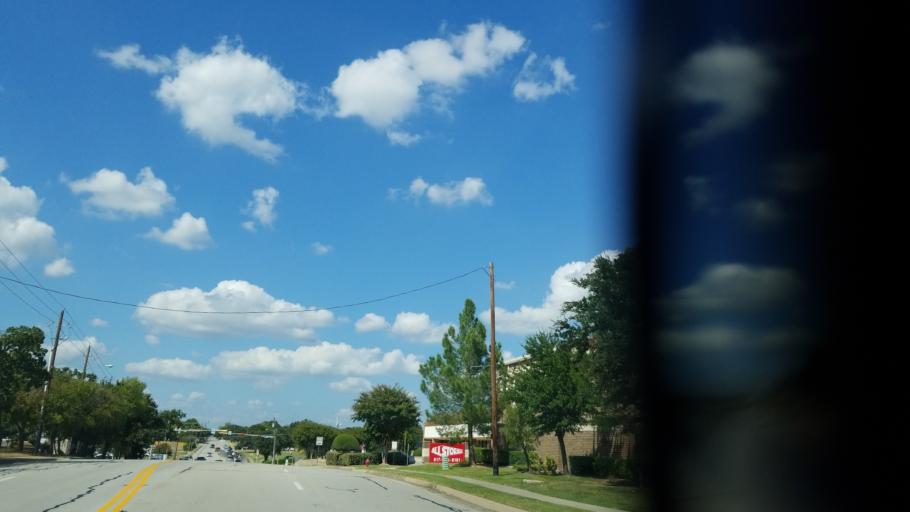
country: US
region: Texas
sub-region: Tarrant County
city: Bedford
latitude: 32.8506
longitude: -97.1170
